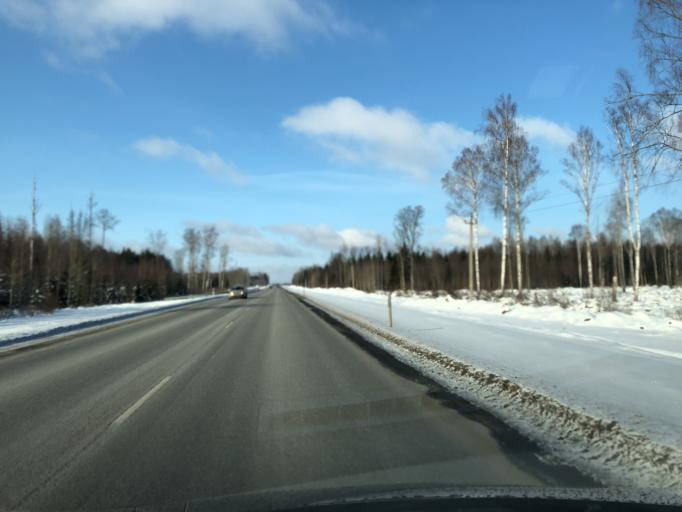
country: EE
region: Tartu
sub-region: Puhja vald
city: Puhja
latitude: 58.4531
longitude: 26.4146
